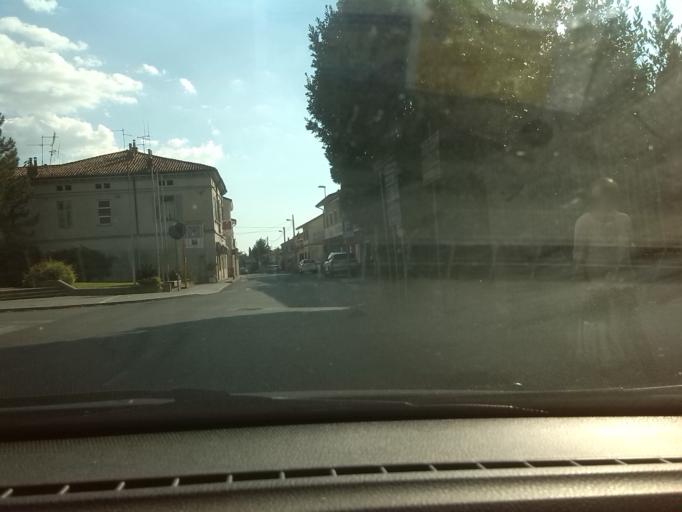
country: IT
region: Friuli Venezia Giulia
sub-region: Provincia di Gorizia
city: Gorizia
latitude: 45.9228
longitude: 13.6025
